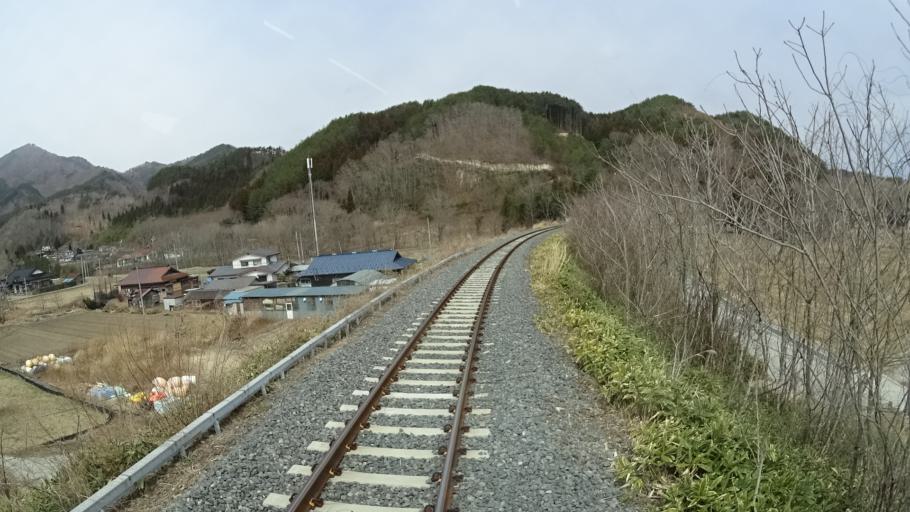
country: JP
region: Iwate
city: Yamada
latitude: 39.5109
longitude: 141.9142
